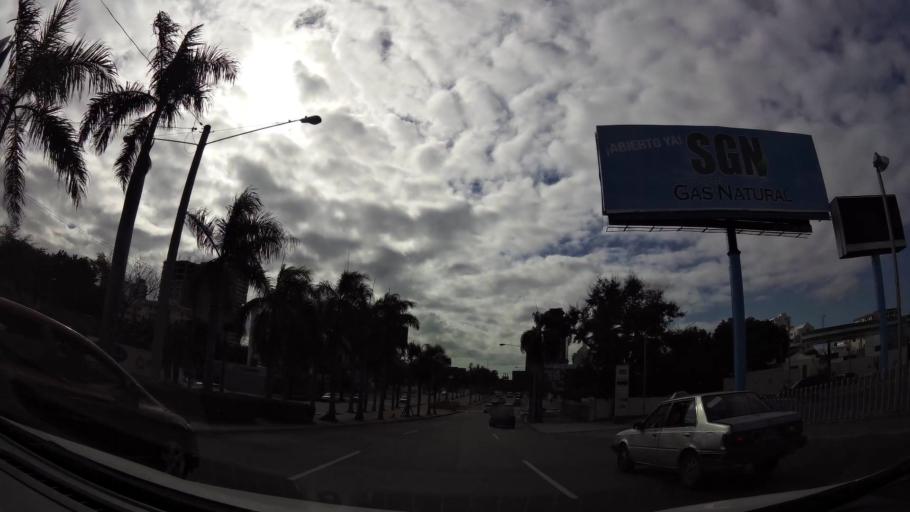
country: DO
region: Nacional
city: La Julia
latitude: 18.4617
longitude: -69.9352
